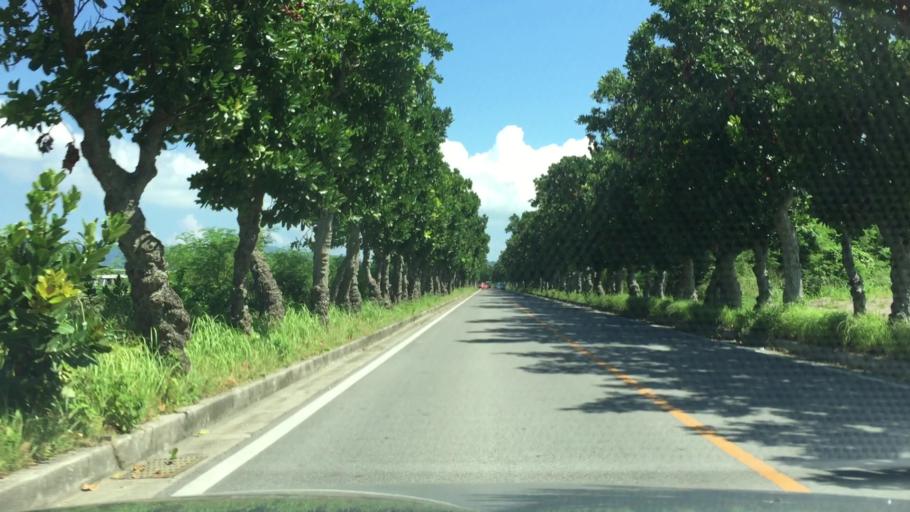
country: JP
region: Okinawa
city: Ishigaki
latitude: 24.3660
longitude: 124.2465
